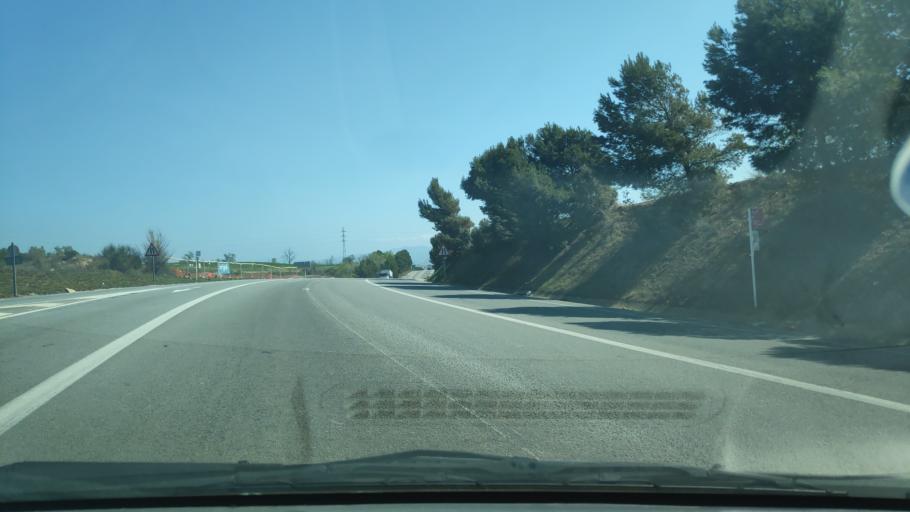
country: ES
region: Catalonia
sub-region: Provincia de Barcelona
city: Barbera del Valles
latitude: 41.5312
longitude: 2.1344
